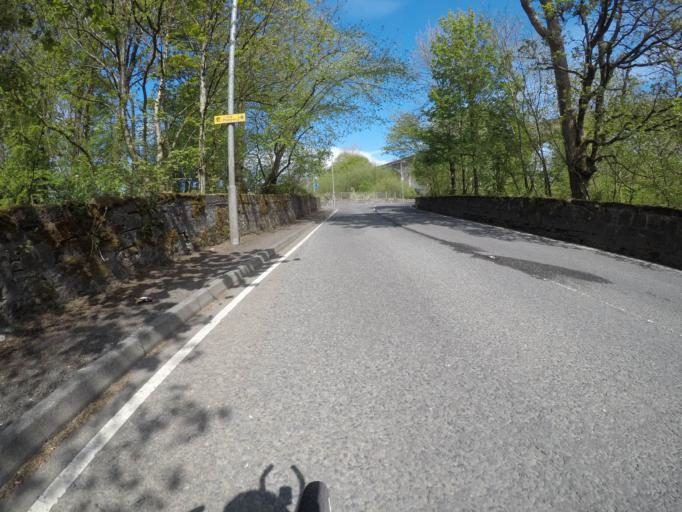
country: GB
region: Scotland
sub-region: East Ayrshire
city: Stewarton
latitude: 55.6773
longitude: -4.5207
